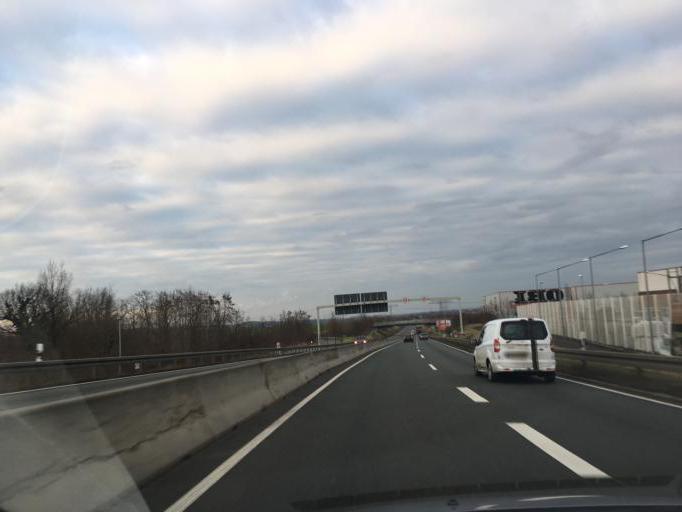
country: DE
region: Thuringia
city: Gerstenberg
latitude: 51.0138
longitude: 12.4540
